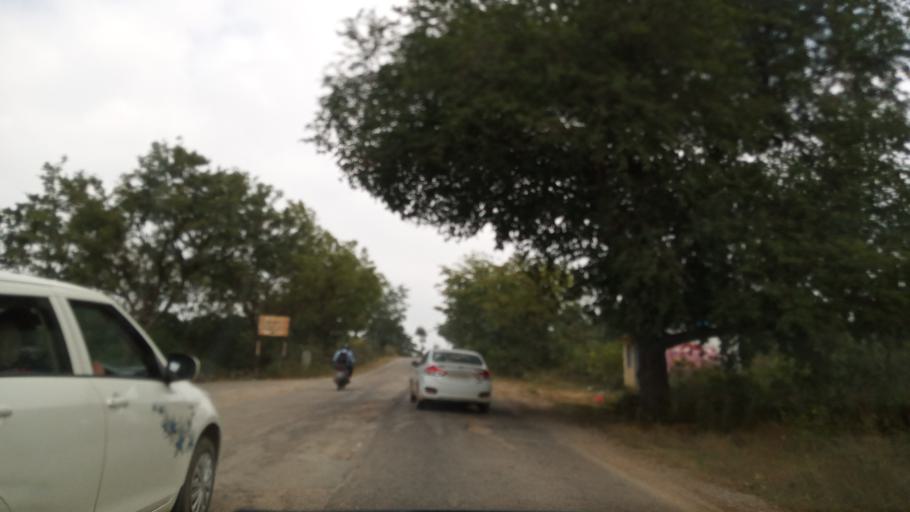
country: IN
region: Andhra Pradesh
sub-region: Chittoor
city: Madanapalle
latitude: 13.5100
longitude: 78.3363
